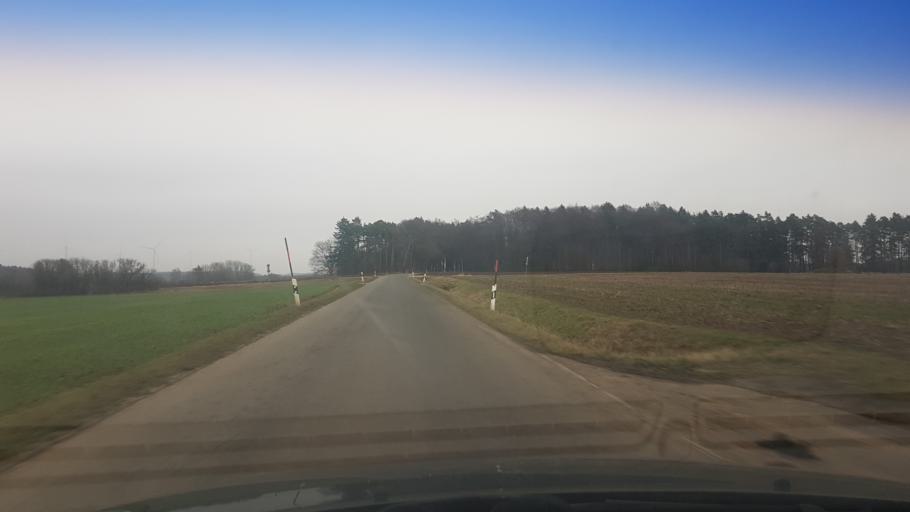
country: DE
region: Bavaria
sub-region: Upper Franconia
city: Weismain
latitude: 50.0301
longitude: 11.2515
